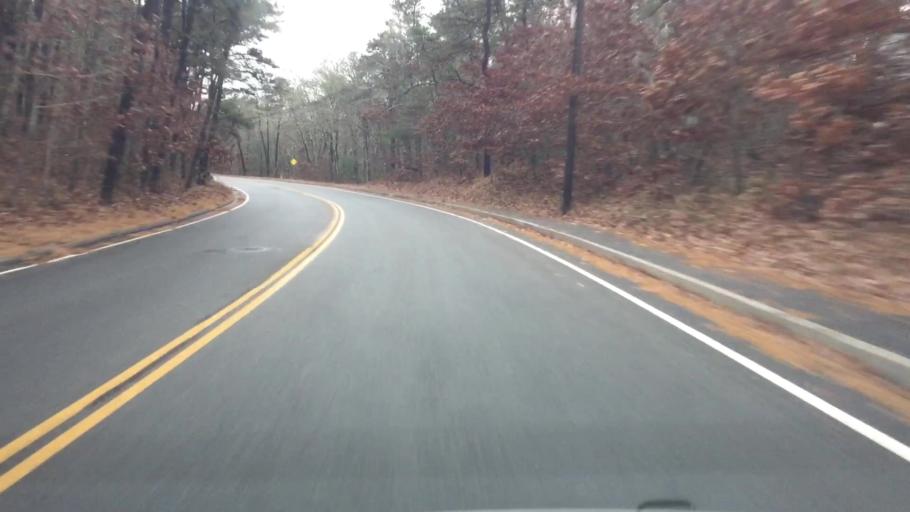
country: US
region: Massachusetts
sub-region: Barnstable County
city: North Falmouth
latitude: 41.6334
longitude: -70.6326
